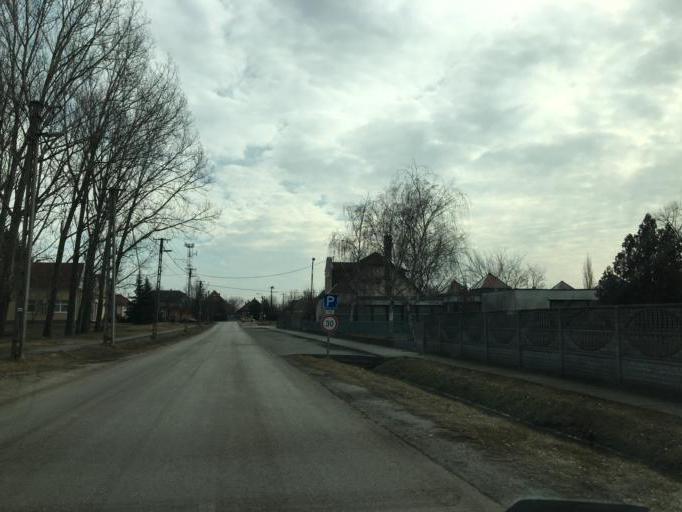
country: HU
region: Pest
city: Szigetcsep
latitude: 47.2653
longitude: 18.9680
